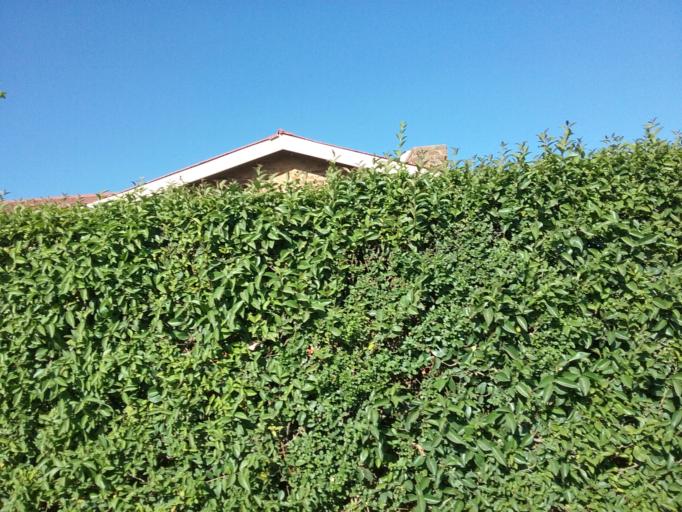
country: LS
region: Maseru
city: Maseru
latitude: -29.3136
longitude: 27.5007
